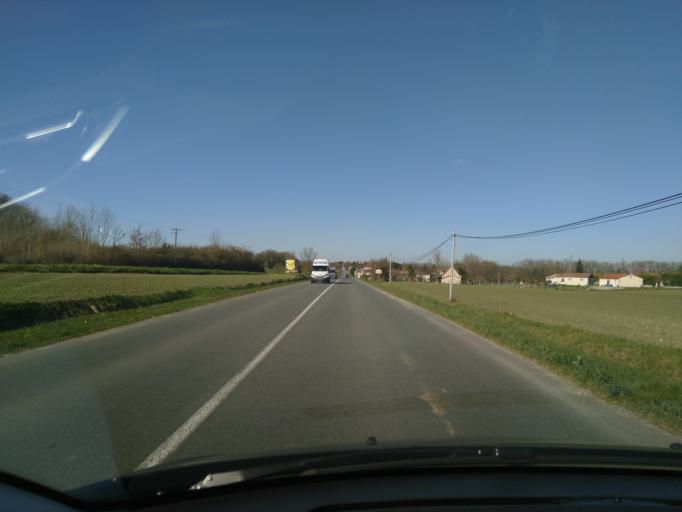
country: FR
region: Aquitaine
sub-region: Departement de la Dordogne
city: Monbazillac
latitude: 44.7496
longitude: 0.5355
